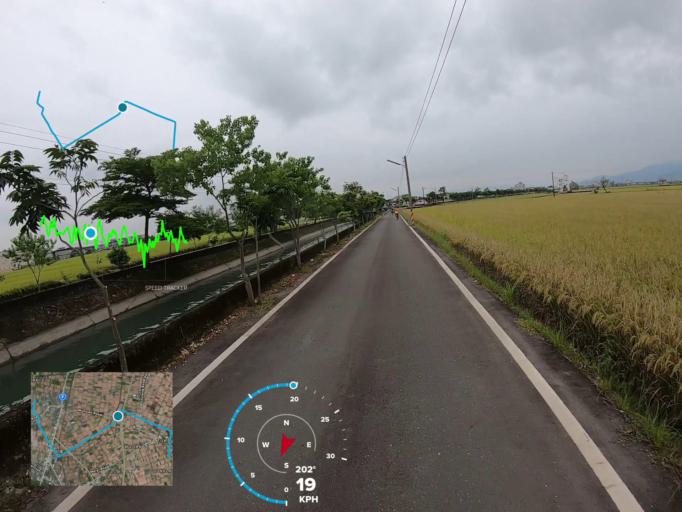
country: TW
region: Taiwan
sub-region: Yilan
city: Yilan
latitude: 24.7820
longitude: 121.7752
